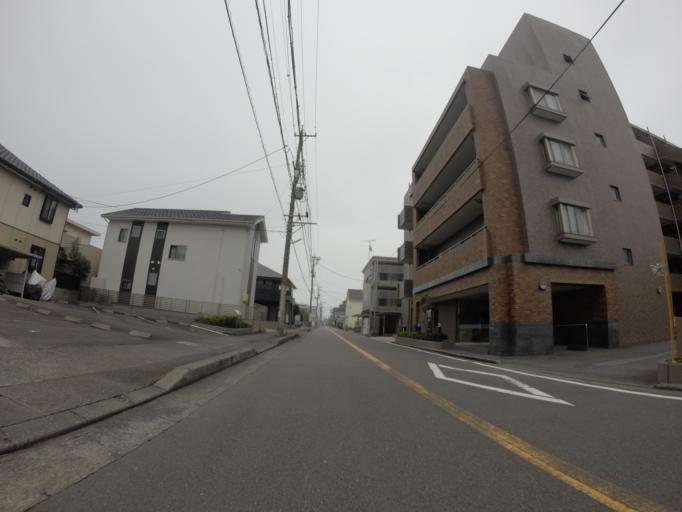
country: JP
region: Shizuoka
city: Shizuoka-shi
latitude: 34.9593
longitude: 138.3972
